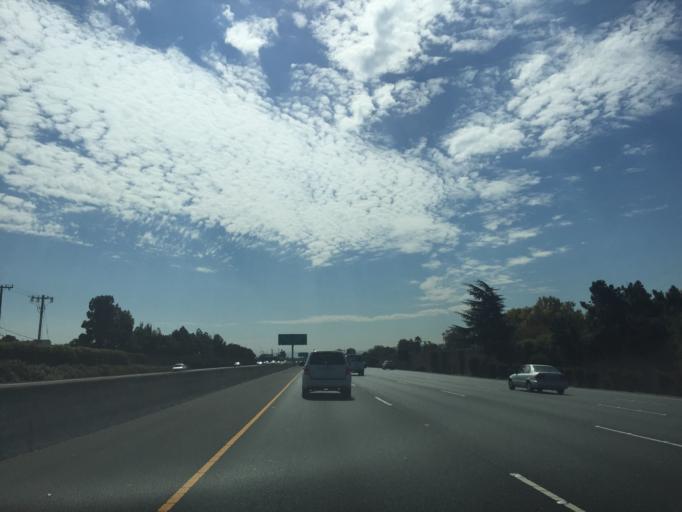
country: US
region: California
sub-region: San Mateo County
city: Belmont
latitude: 37.5391
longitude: -122.2830
